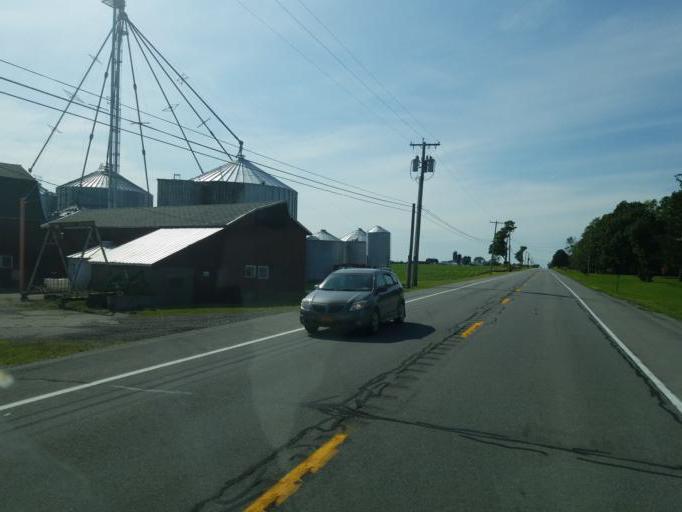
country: US
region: New York
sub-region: Livingston County
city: Caledonia
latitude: 42.9456
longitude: -77.8214
